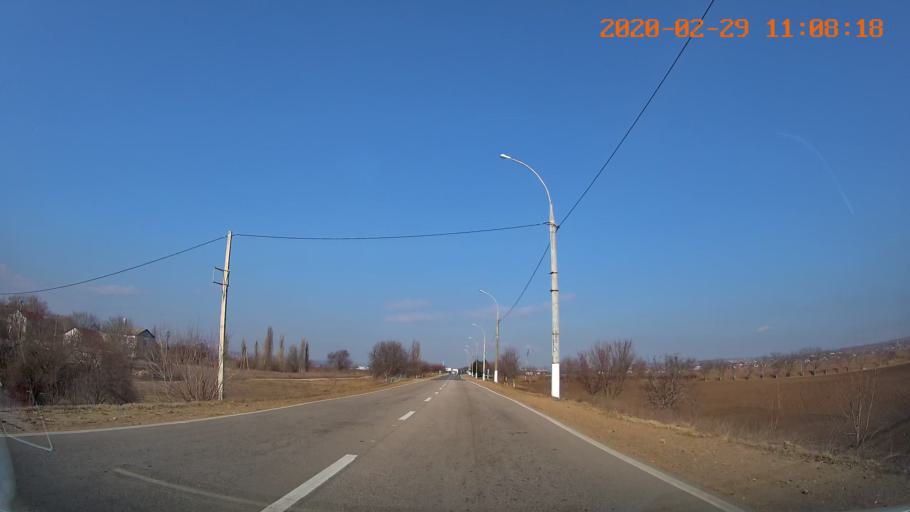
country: MD
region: Criuleni
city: Criuleni
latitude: 47.2328
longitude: 29.1765
